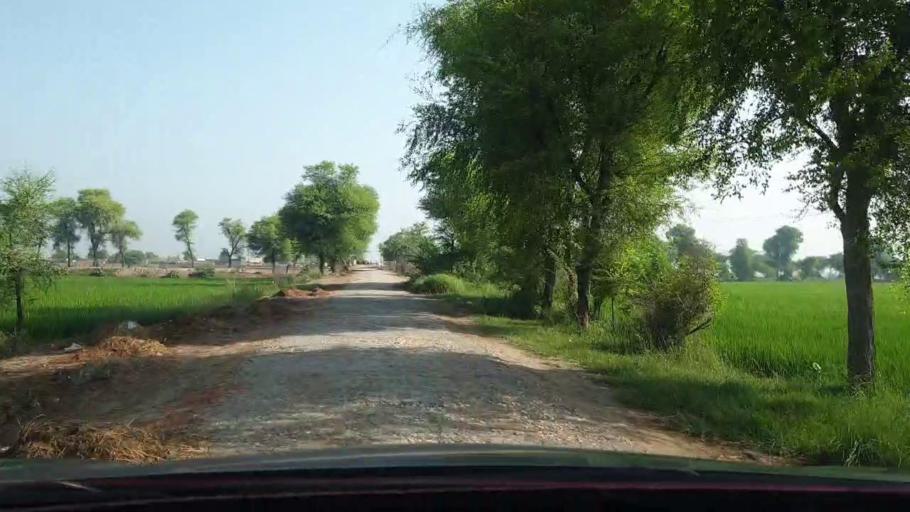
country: PK
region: Sindh
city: Nasirabad
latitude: 27.4480
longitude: 67.9192
